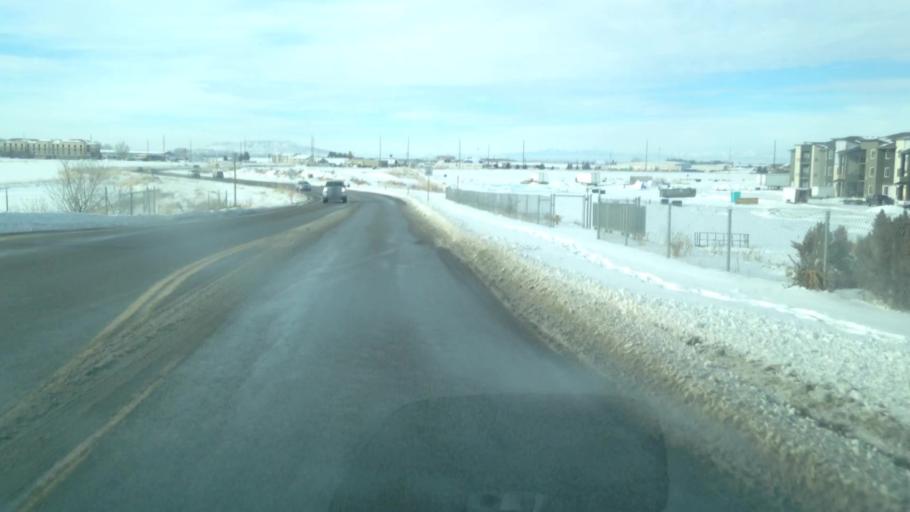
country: US
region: Idaho
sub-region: Madison County
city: Rexburg
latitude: 43.8042
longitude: -111.7990
